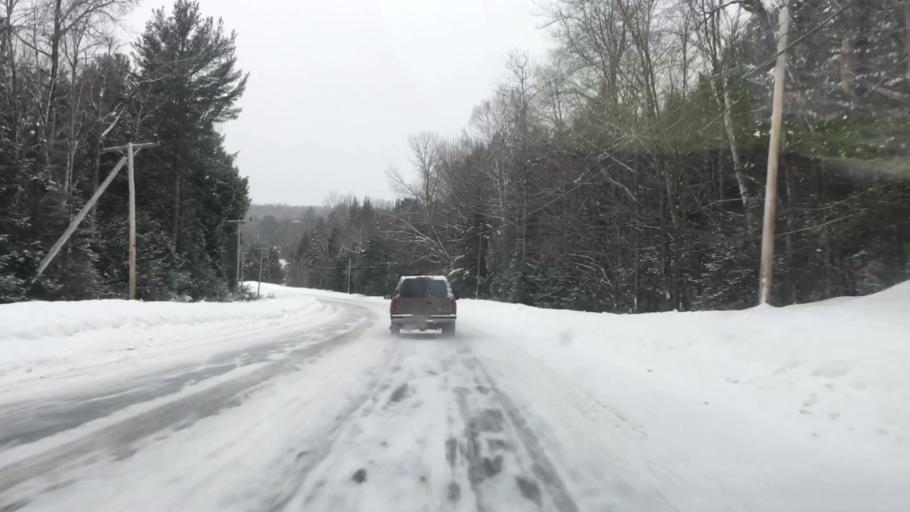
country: US
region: Maine
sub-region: Penobscot County
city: Medway
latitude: 45.6000
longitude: -68.4635
